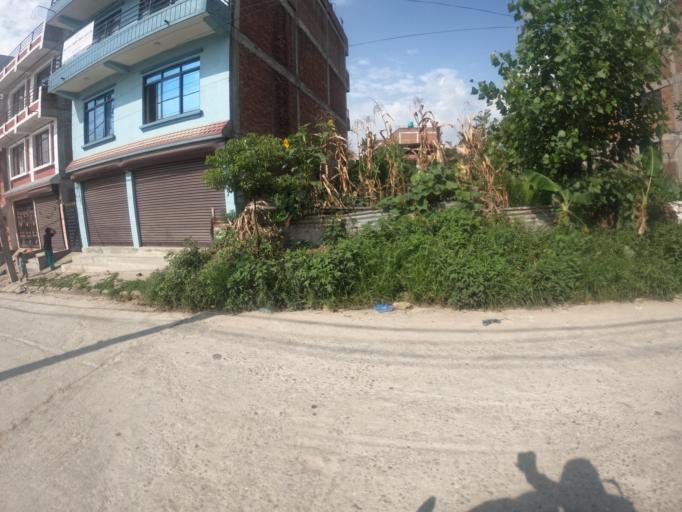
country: NP
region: Central Region
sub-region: Bagmati Zone
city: Bhaktapur
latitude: 27.6750
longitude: 85.4430
